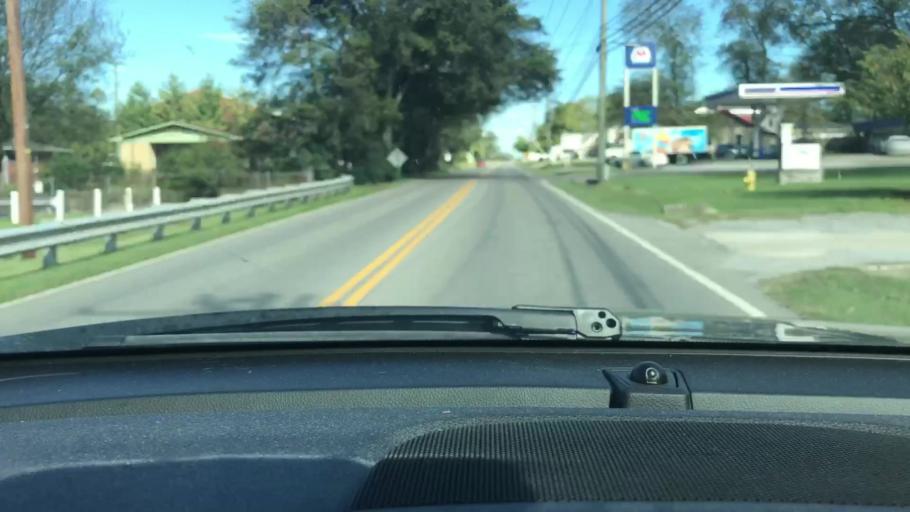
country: US
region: Tennessee
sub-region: Sumner County
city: Hendersonville
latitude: 36.2997
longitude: -86.6206
